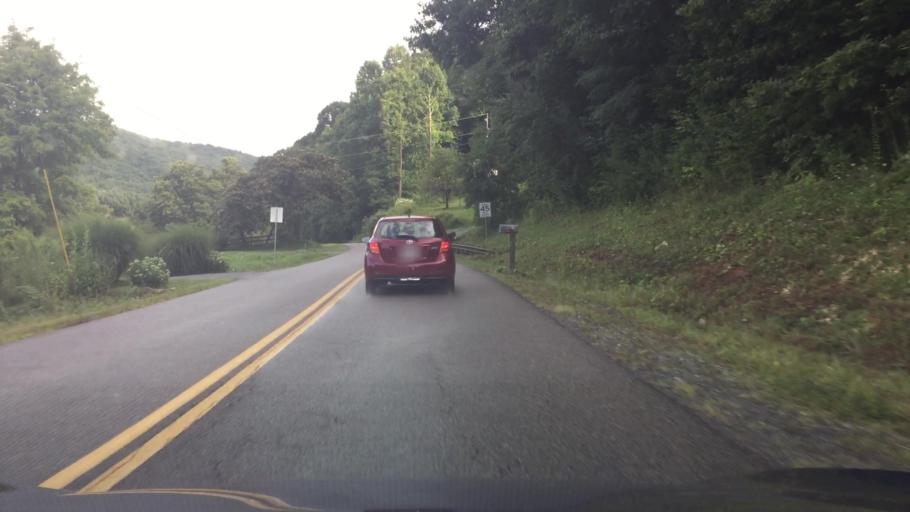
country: US
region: Virginia
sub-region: Smyth County
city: Atkins
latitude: 36.8407
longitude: -81.4221
